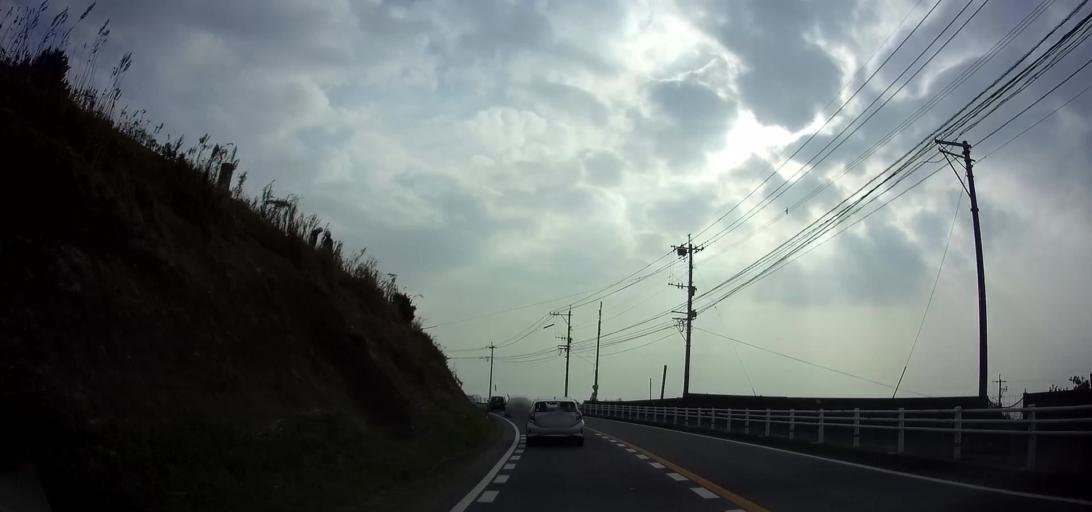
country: JP
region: Nagasaki
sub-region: Isahaya-shi
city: Isahaya
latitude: 32.7903
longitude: 130.0663
